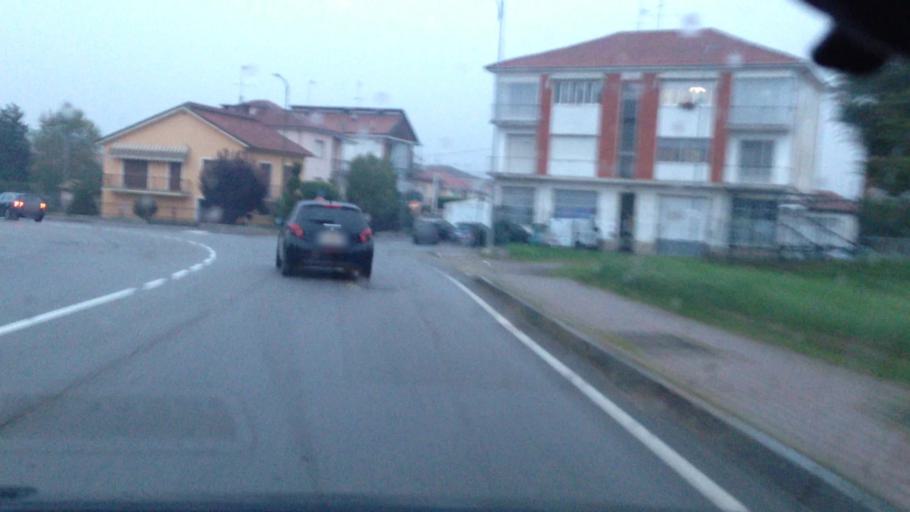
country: IT
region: Piedmont
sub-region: Provincia di Asti
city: Asti
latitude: 44.9138
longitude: 8.2183
